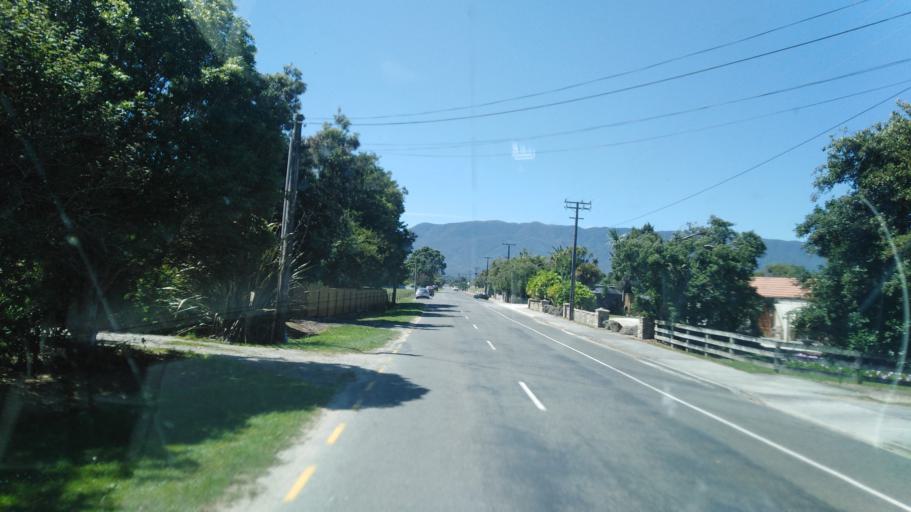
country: NZ
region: West Coast
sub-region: Buller District
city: Westport
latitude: -41.2491
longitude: 172.1192
